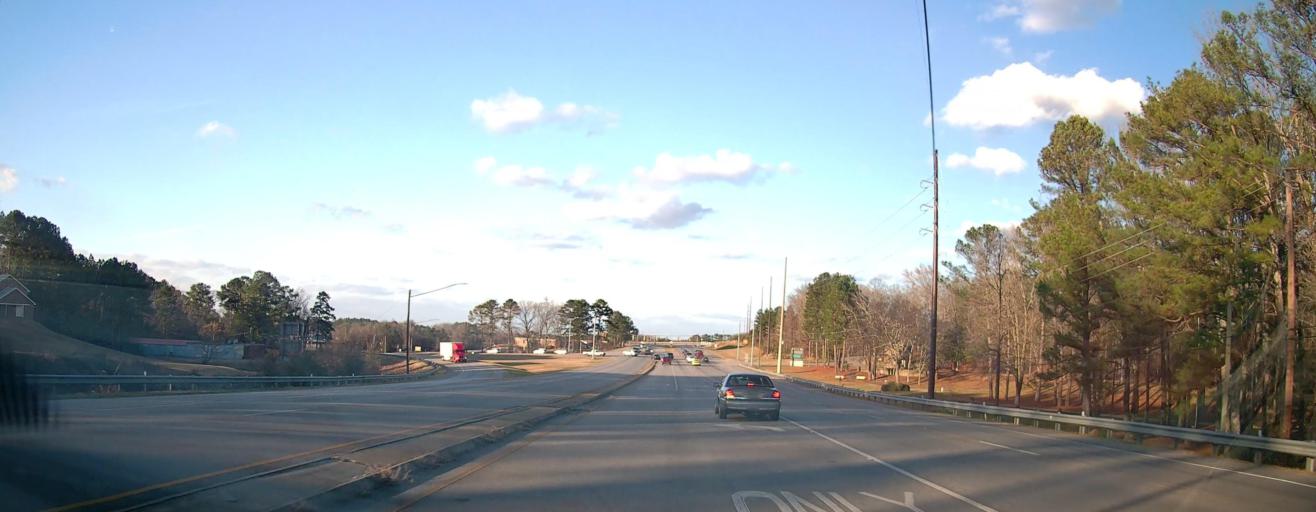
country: US
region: Alabama
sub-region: Calhoun County
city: Saks
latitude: 33.6940
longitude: -85.8233
